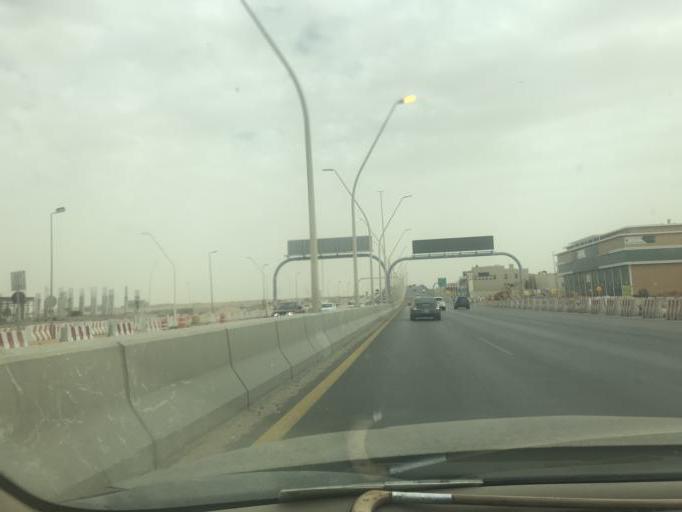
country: SA
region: Ar Riyad
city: Riyadh
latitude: 24.8319
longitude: 46.6589
